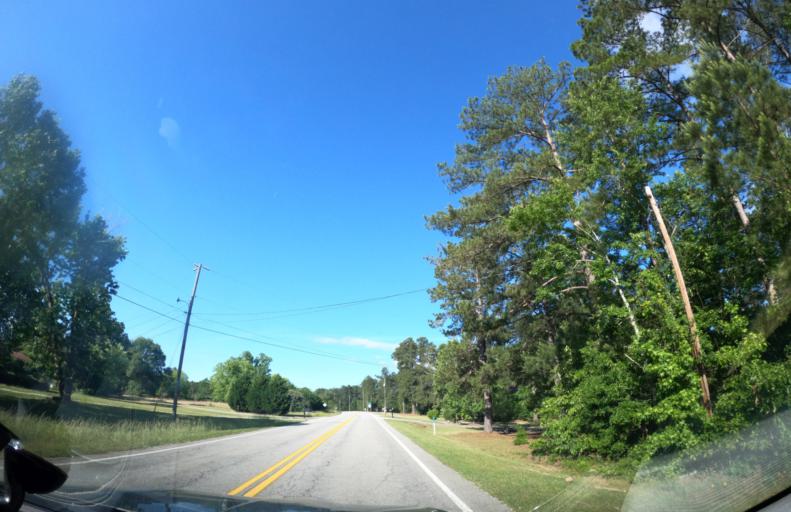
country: US
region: Georgia
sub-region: Columbia County
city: Harlem
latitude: 33.4272
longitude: -82.2968
